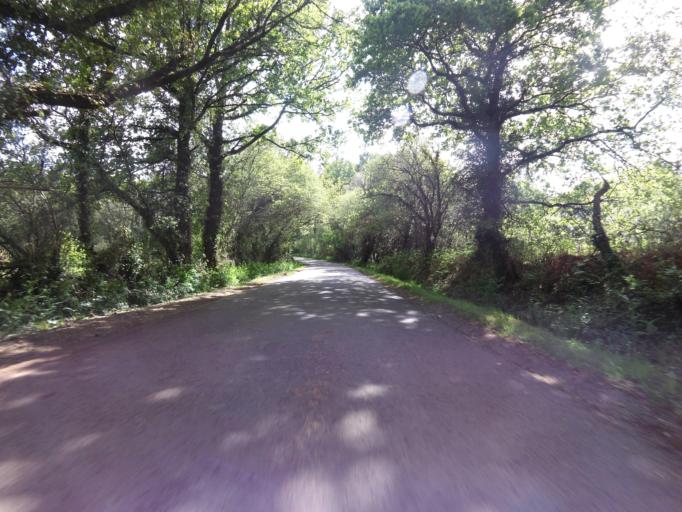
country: FR
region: Brittany
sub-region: Departement du Morbihan
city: Plougoumelen
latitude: 47.6492
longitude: -2.8952
